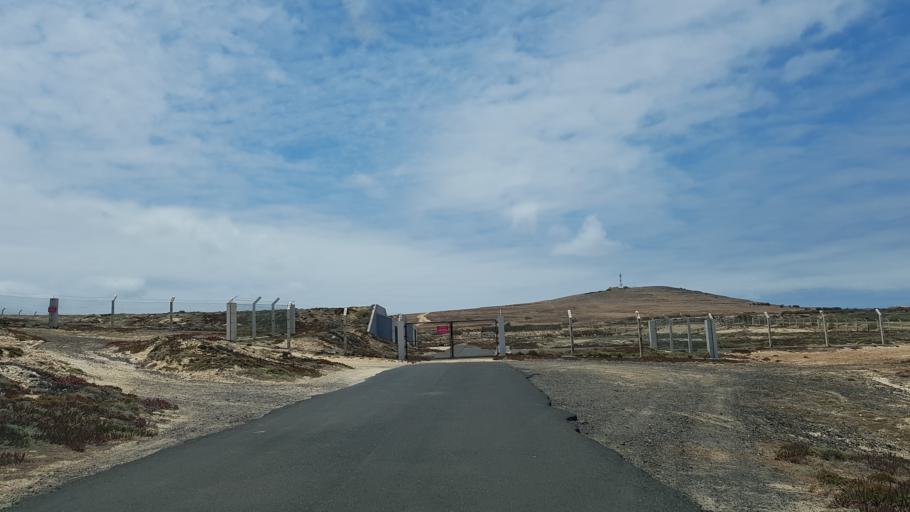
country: PT
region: Madeira
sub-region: Porto Santo
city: Camacha
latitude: 33.0821
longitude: -16.3590
